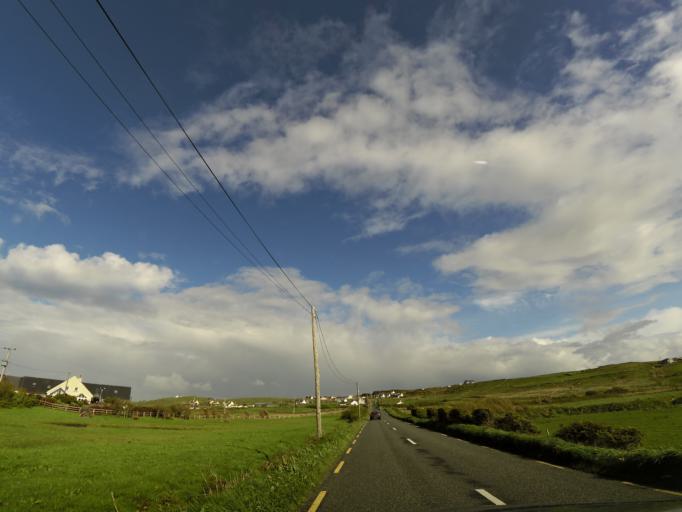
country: IE
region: Connaught
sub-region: County Galway
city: Bearna
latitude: 53.0120
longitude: -9.3679
